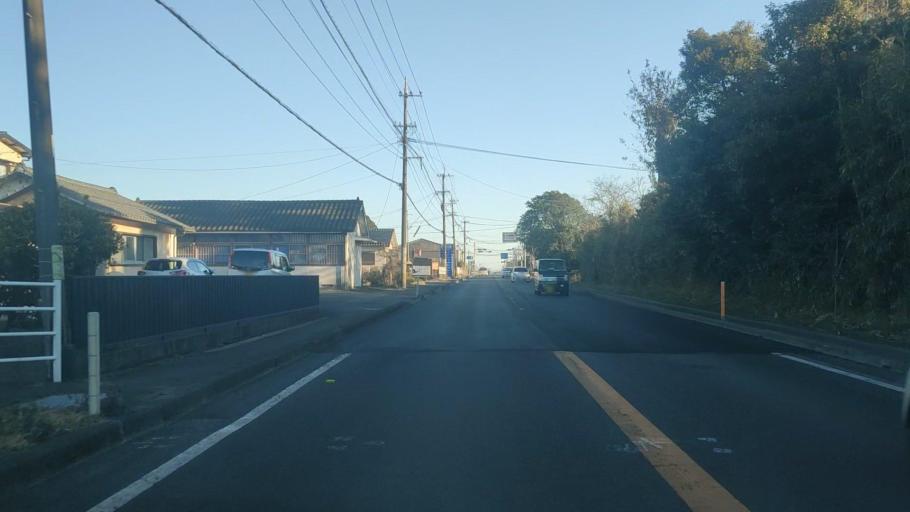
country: JP
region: Miyazaki
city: Takanabe
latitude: 32.2195
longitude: 131.5408
